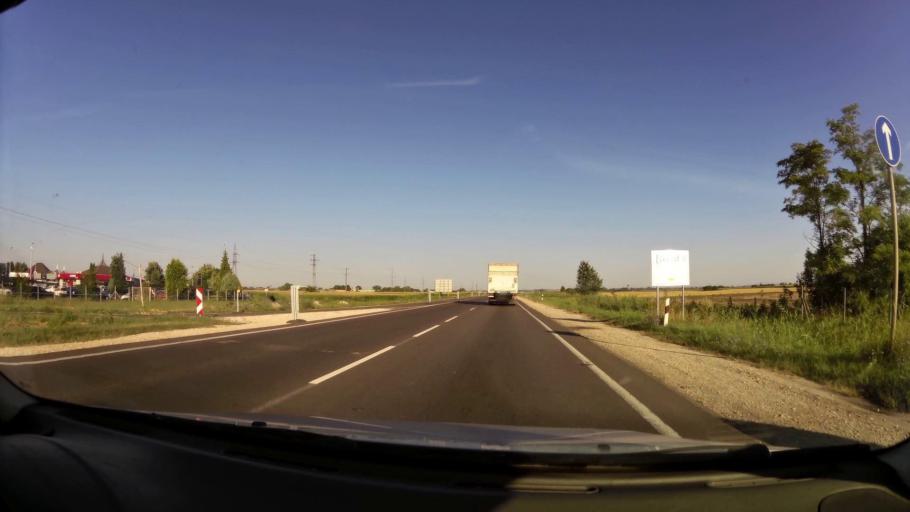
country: HU
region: Pest
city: Cegled
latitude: 47.1969
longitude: 19.8099
